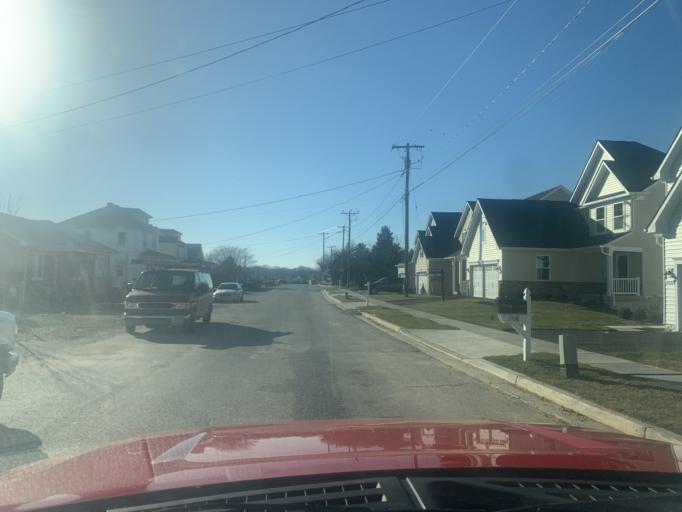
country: US
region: Maryland
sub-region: Anne Arundel County
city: Brooklyn Park
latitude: 39.2120
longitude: -76.6093
